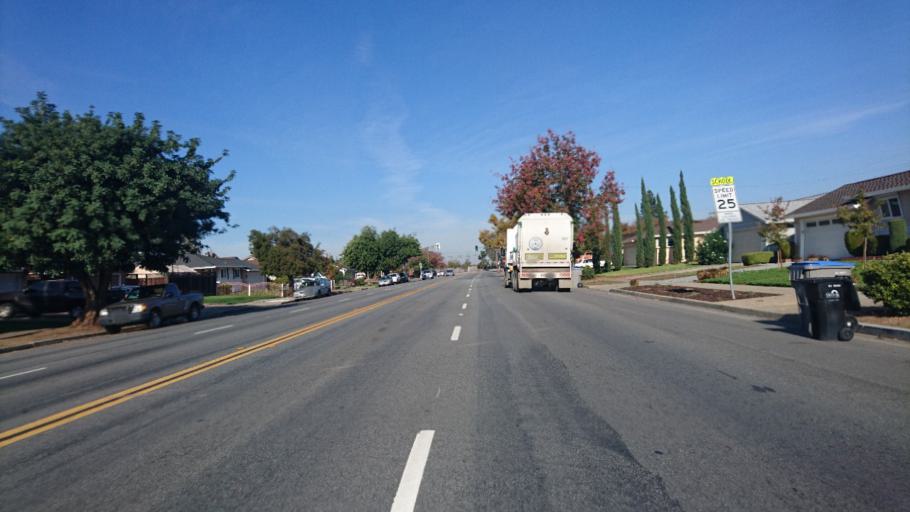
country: US
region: California
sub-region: Santa Clara County
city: Cambrian Park
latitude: 37.2480
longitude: -121.8938
